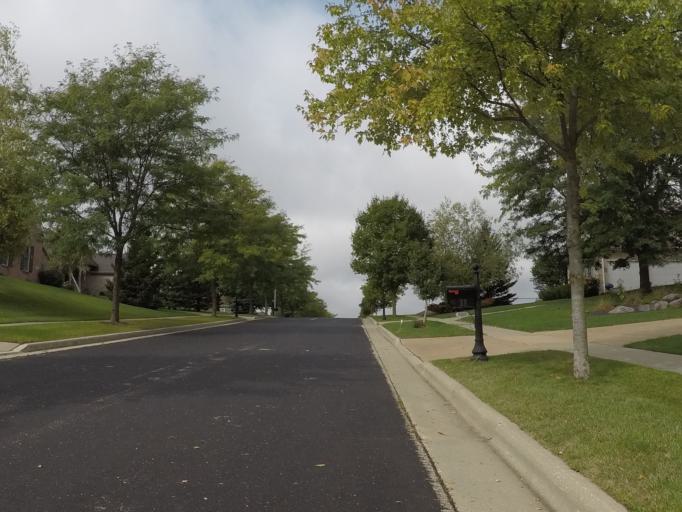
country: US
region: Wisconsin
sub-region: Dane County
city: Verona
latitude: 43.0416
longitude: -89.5447
